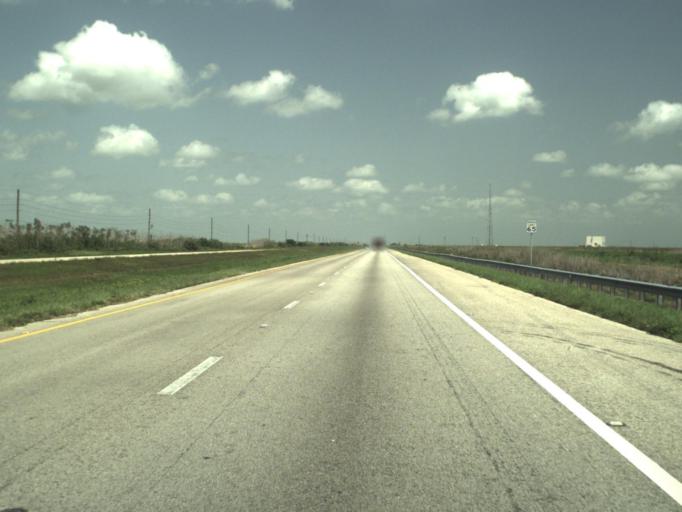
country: US
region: Florida
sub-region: Palm Beach County
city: Belle Glade Camp
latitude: 26.4222
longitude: -80.6051
